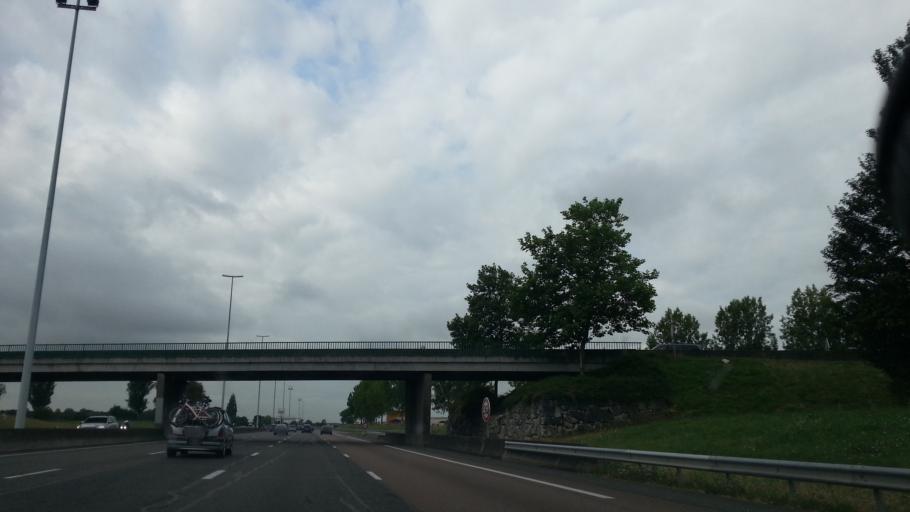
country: FR
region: Bourgogne
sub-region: Departement de la Cote-d'Or
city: Bligny-les-Beaune
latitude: 47.0007
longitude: 4.8597
